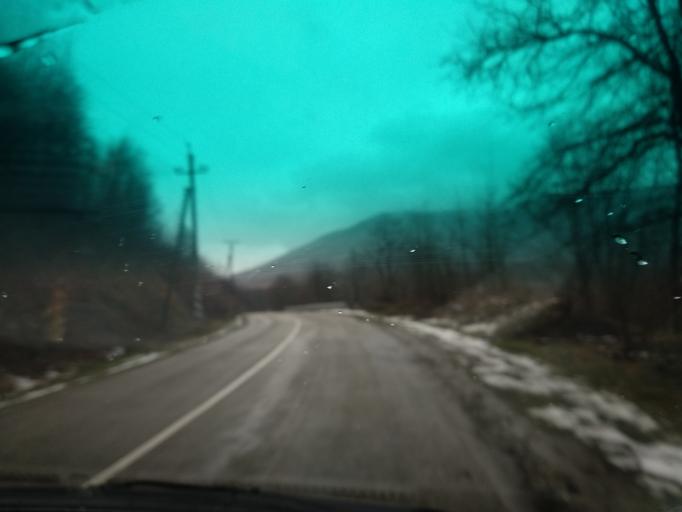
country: RU
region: Krasnodarskiy
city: Khadyzhensk
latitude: 44.2229
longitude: 39.3895
